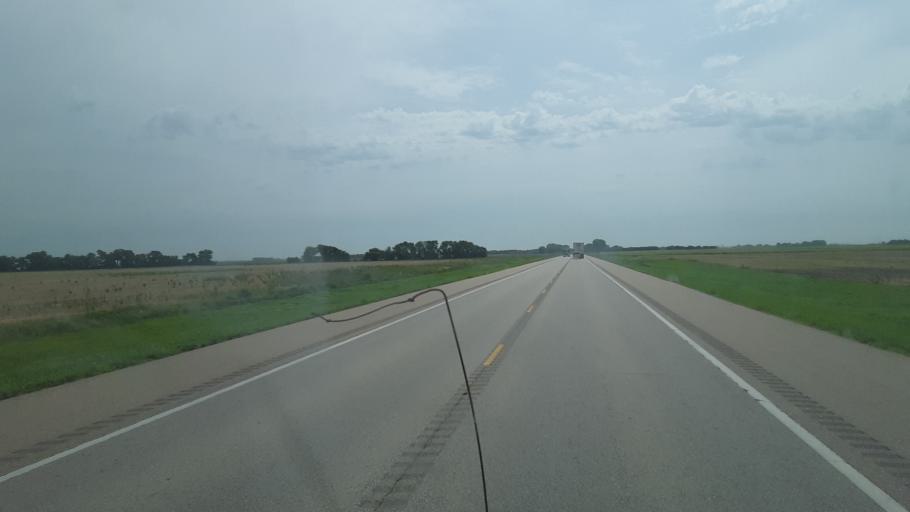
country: US
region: Kansas
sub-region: Reno County
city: Nickerson
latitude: 37.9848
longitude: -98.2032
